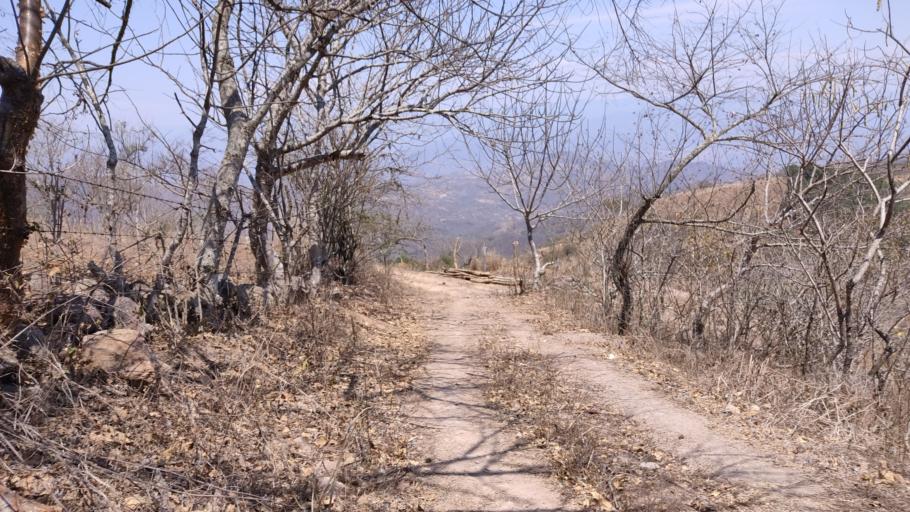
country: MX
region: Nayarit
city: Puga
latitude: 21.6230
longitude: -104.7116
